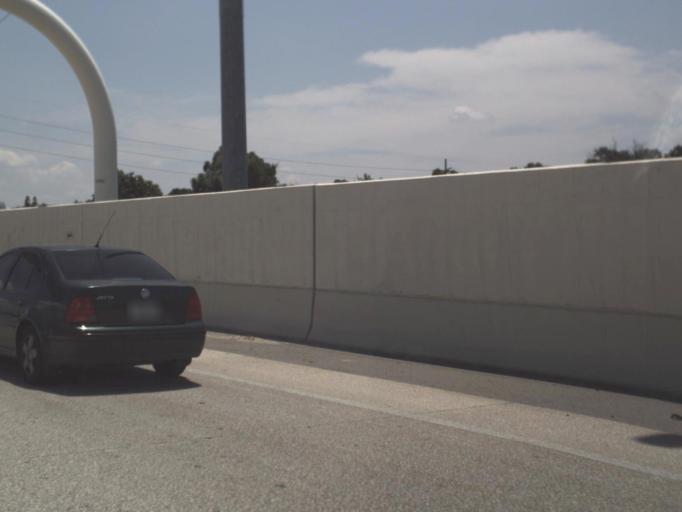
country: US
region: Florida
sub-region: Hillsborough County
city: Tampa
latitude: 27.9556
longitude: -82.4945
